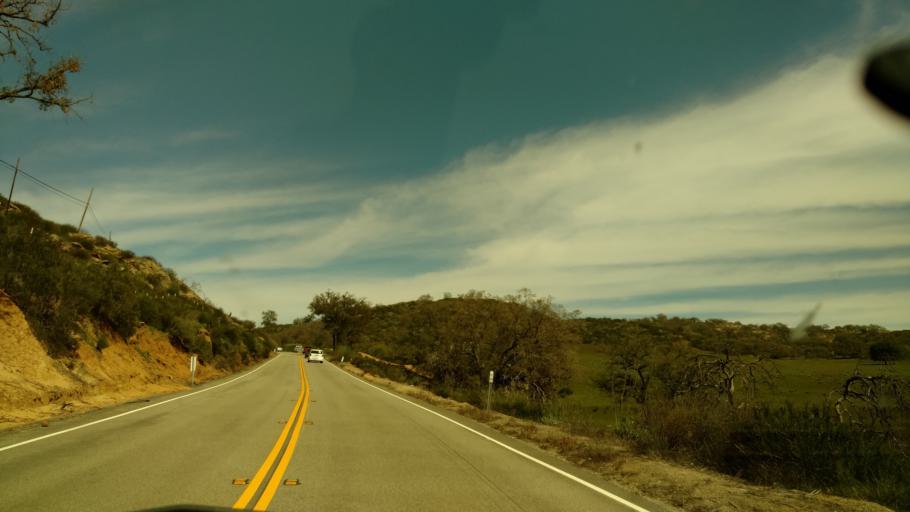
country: US
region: California
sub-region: San Diego County
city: San Diego Country Estates
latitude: 33.0695
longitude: -116.7207
